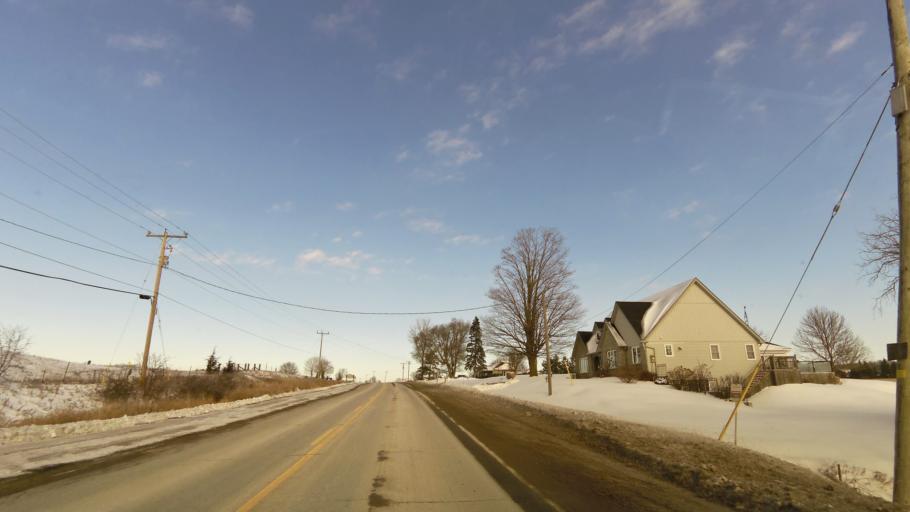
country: CA
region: Ontario
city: Quinte West
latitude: 44.1353
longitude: -77.7870
